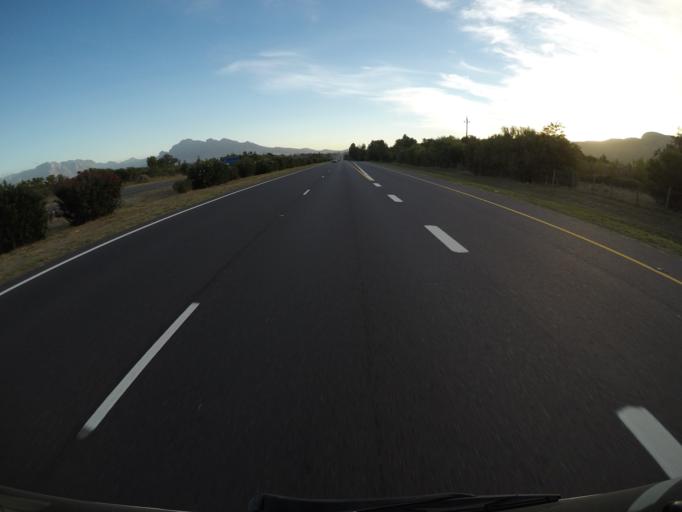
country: ZA
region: Western Cape
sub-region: Cape Winelands District Municipality
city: Paarl
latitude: -33.7544
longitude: 18.9869
